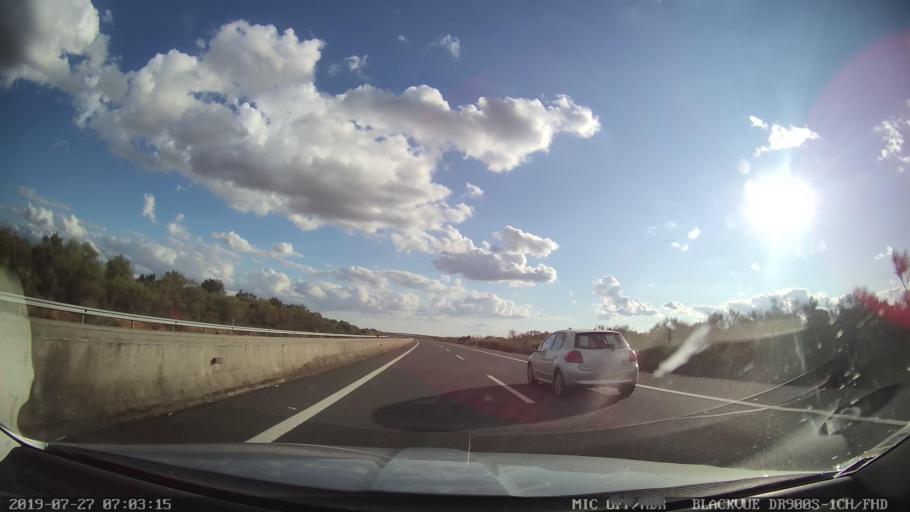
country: ES
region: Extremadura
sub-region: Provincia de Caceres
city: Casas de Miravete
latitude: 39.6784
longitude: -5.7370
